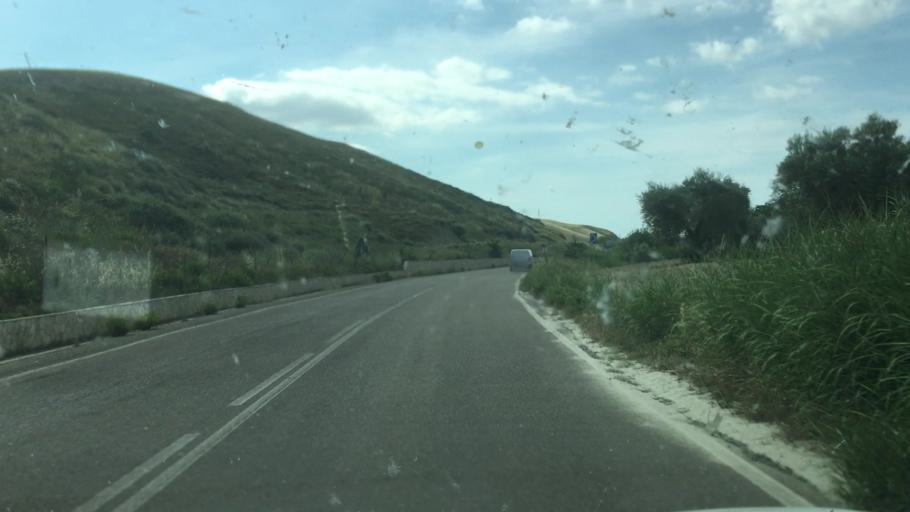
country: IT
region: Basilicate
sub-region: Provincia di Matera
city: Salandra
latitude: 40.5331
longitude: 16.2868
